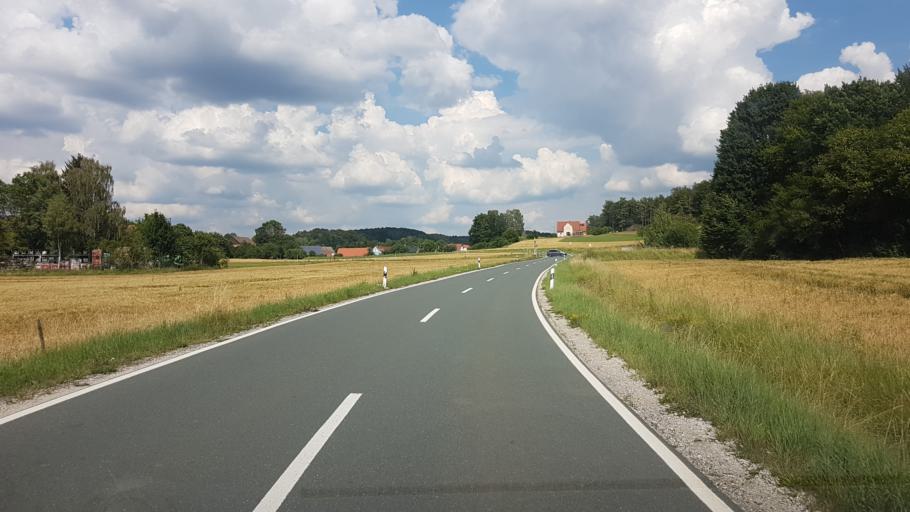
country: DE
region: Bavaria
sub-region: Upper Franconia
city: Egloffstein
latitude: 49.7506
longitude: 11.2613
